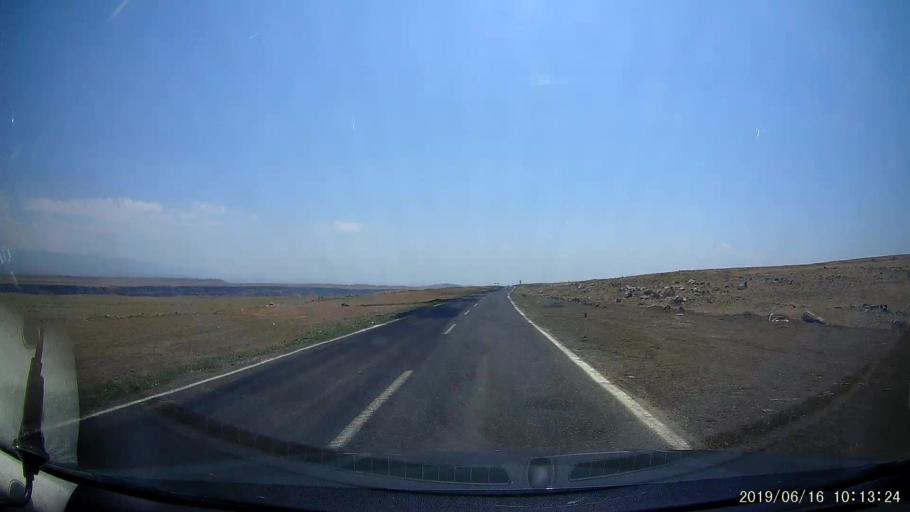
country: TR
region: Igdir
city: Tuzluca
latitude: 40.1927
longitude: 43.6419
